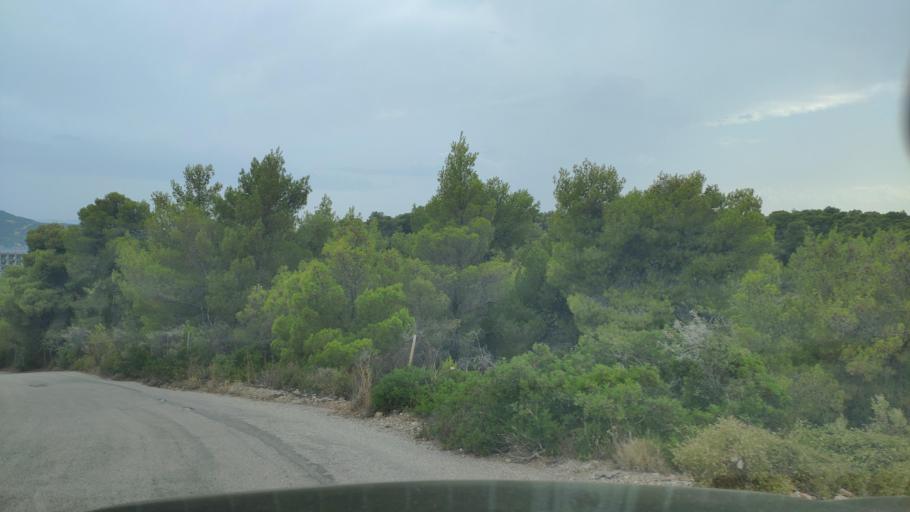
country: GR
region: Peloponnese
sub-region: Nomos Argolidos
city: Porto Cheli
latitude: 37.3099
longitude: 23.1475
